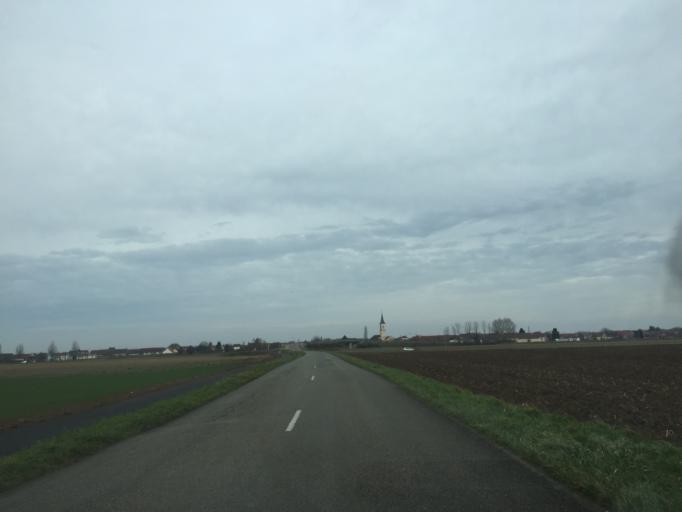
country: FR
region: Franche-Comte
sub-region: Departement du Jura
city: Tavaux
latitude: 47.0283
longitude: 5.4113
